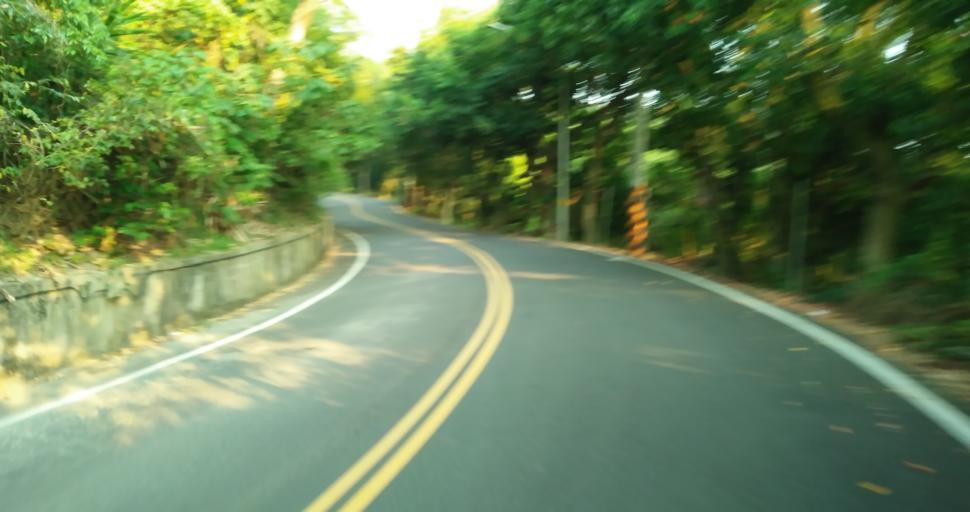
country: TW
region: Taiwan
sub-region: Hsinchu
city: Hsinchu
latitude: 24.7756
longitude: 120.9744
